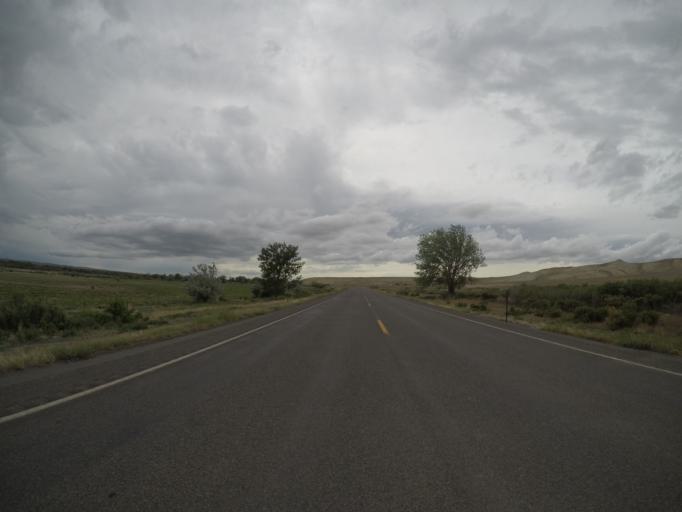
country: US
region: Wyoming
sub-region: Big Horn County
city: Lovell
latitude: 44.8771
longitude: -108.3018
